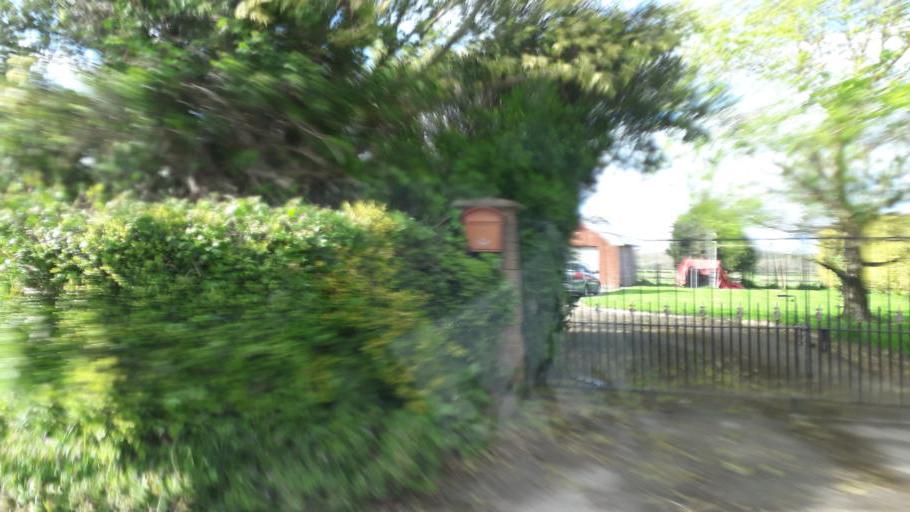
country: IE
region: Leinster
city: Ballymun
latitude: 53.4473
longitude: -6.2727
